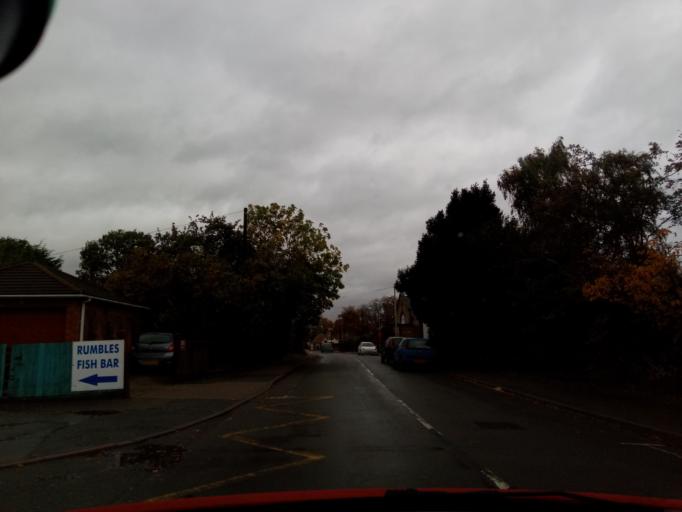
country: GB
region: England
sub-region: Cambridgeshire
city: Sawtry
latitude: 52.4372
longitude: -0.2842
